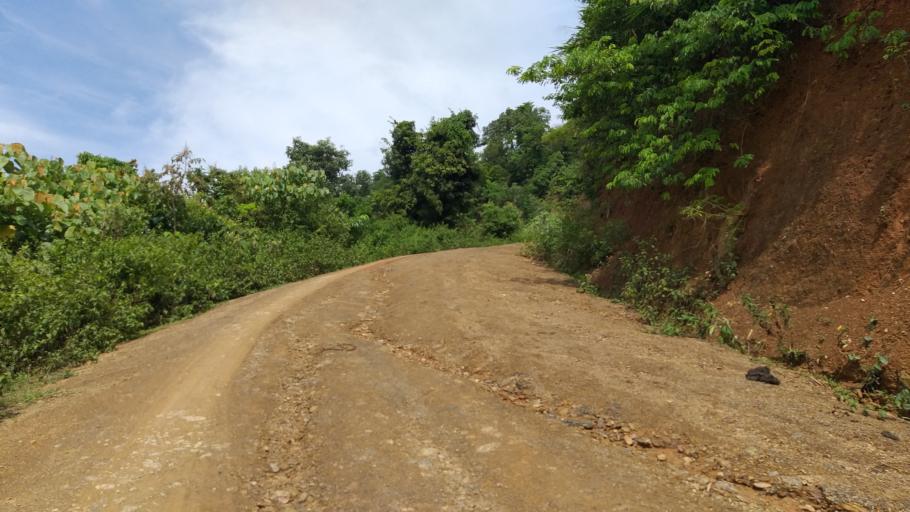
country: VN
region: Huyen Dien Bien
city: Dien Bien Phu
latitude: 21.4338
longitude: 102.6809
